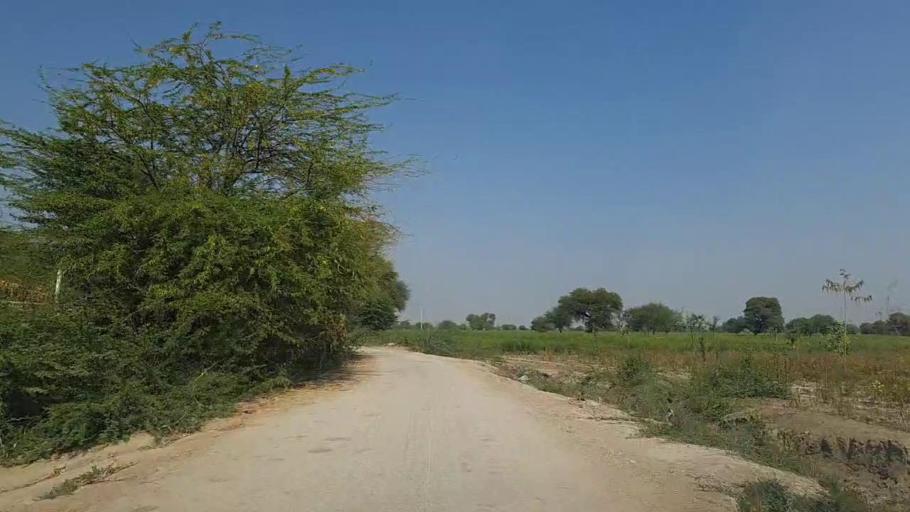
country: PK
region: Sindh
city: Naukot
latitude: 24.8733
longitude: 69.3844
